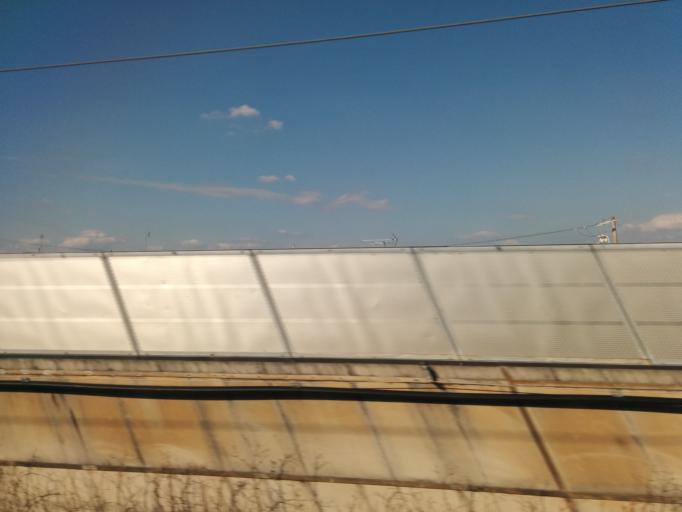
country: JP
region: Shizuoka
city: Iwata
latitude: 34.7076
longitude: 137.8631
